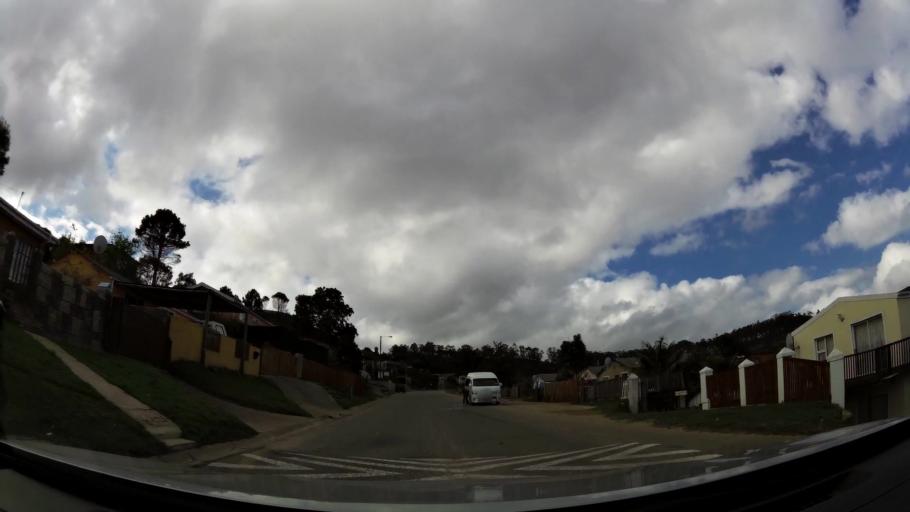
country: ZA
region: Western Cape
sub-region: Eden District Municipality
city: Knysna
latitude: -34.0515
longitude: 23.1001
